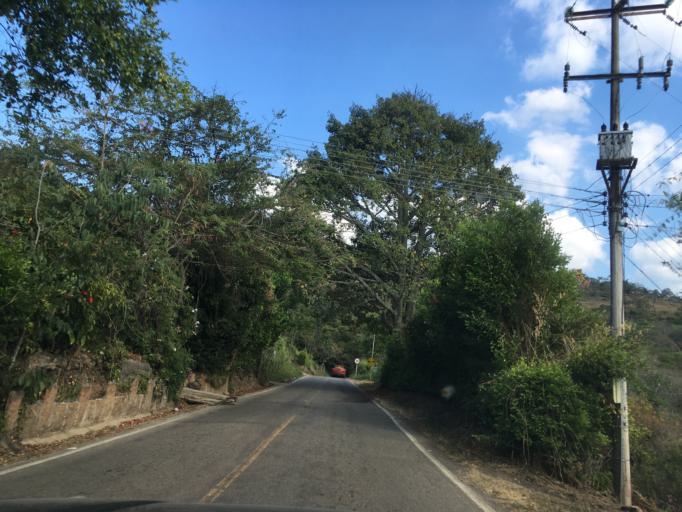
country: CO
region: Santander
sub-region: San Gil
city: San Gil
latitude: 6.5743
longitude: -73.1504
